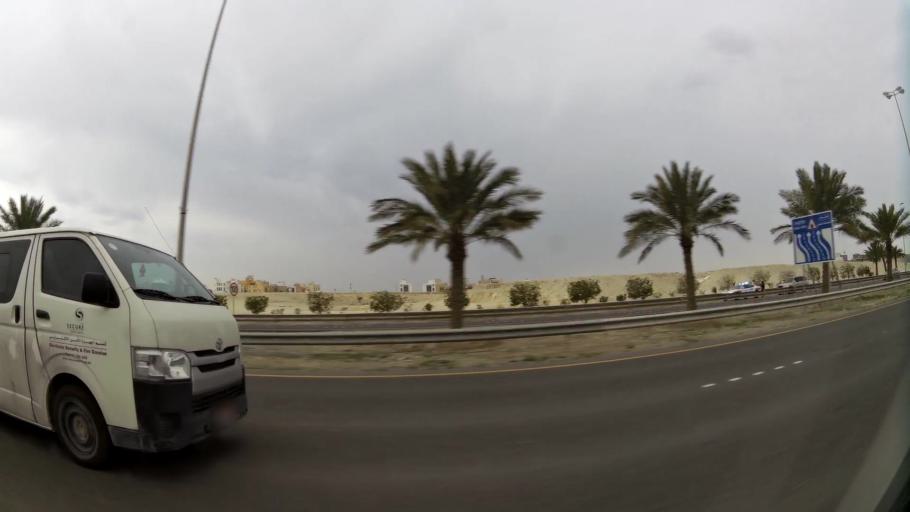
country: BH
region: Central Governorate
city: Madinat Hamad
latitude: 26.0917
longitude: 50.5150
